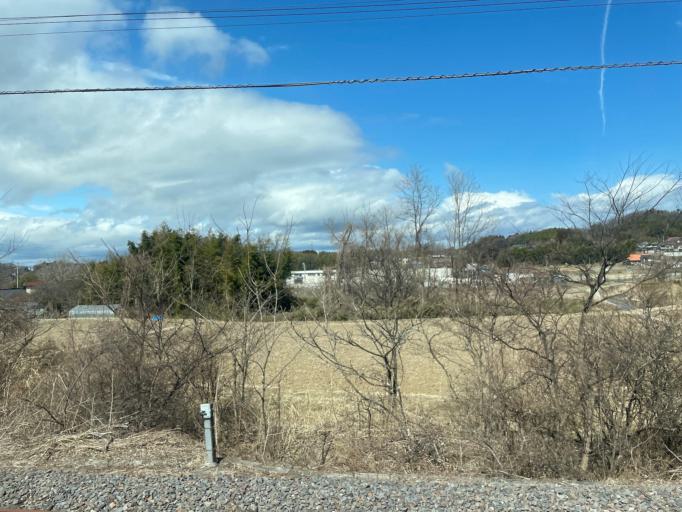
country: JP
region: Fukushima
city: Sukagawa
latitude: 37.3139
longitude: 140.4327
